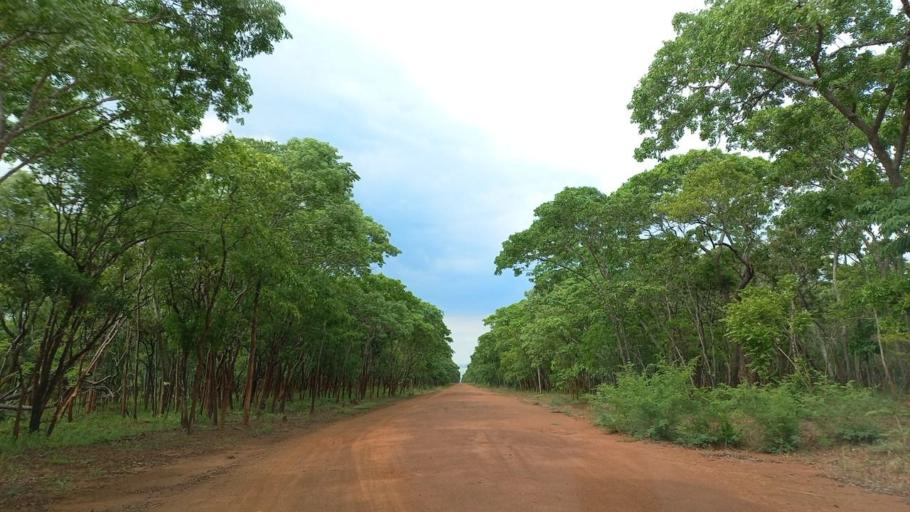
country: ZM
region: North-Western
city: Kalengwa
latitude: -13.4156
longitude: 25.0594
